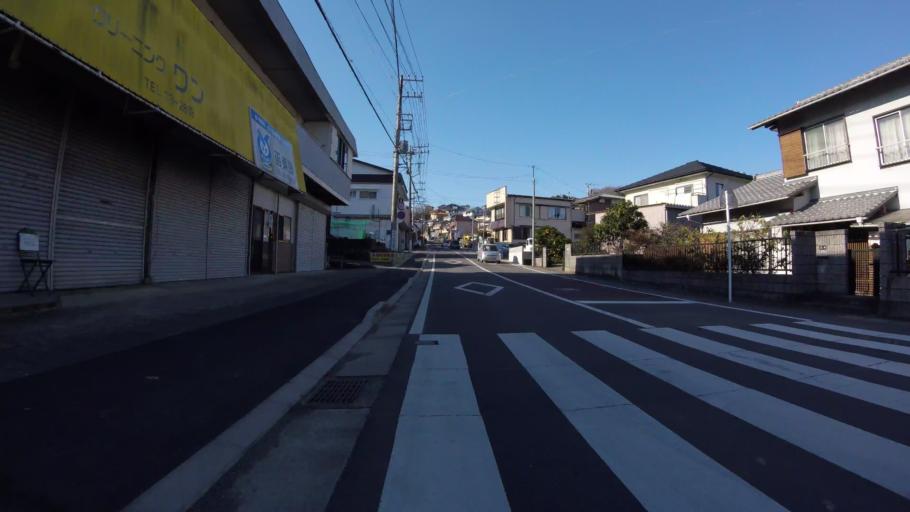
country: JP
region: Shizuoka
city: Mishima
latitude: 35.0876
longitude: 138.9662
